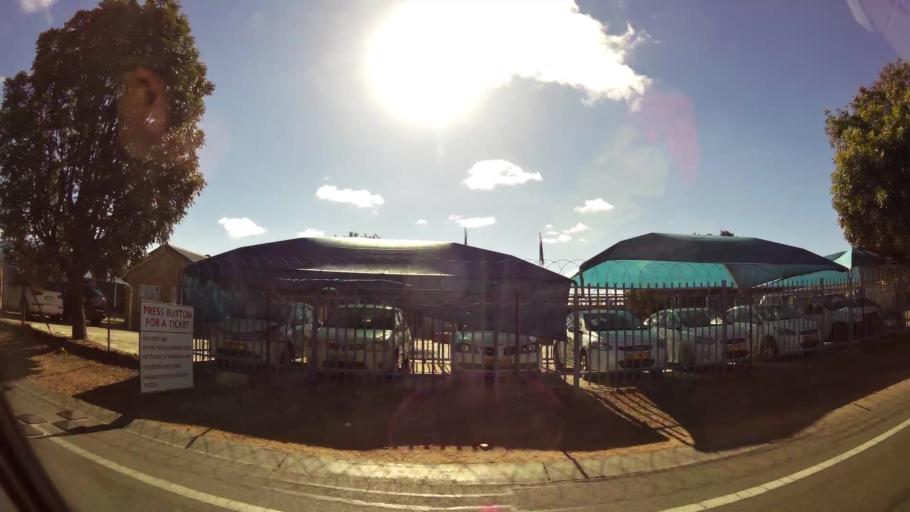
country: ZA
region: Limpopo
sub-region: Capricorn District Municipality
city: Polokwane
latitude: -23.8609
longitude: 29.4531
